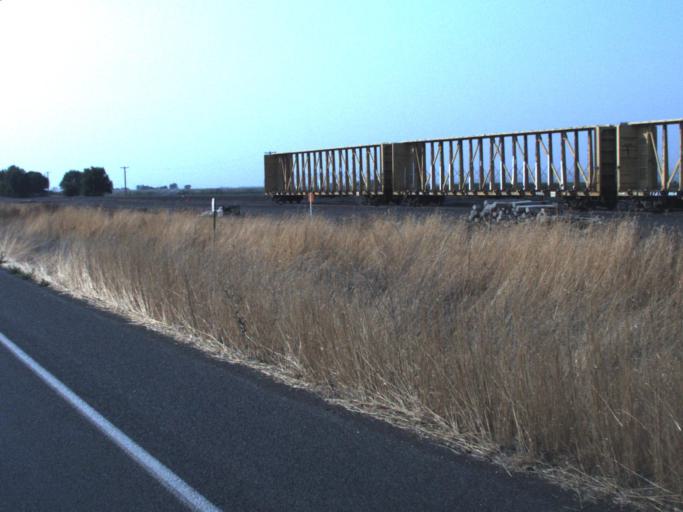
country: US
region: Washington
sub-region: Yakima County
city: Mabton
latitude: 46.2140
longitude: -120.0093
